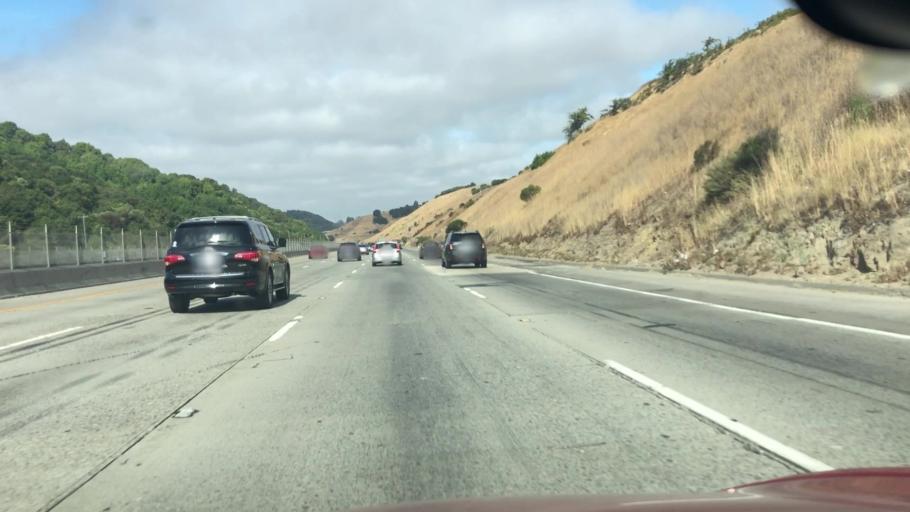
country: US
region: California
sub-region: Alameda County
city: Fairview
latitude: 37.7037
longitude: -122.0036
